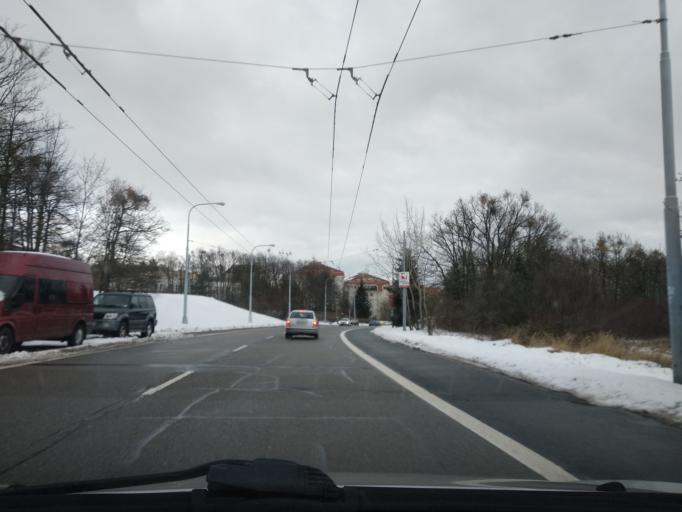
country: CZ
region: South Moravian
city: Troubsko
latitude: 49.1922
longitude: 16.5299
